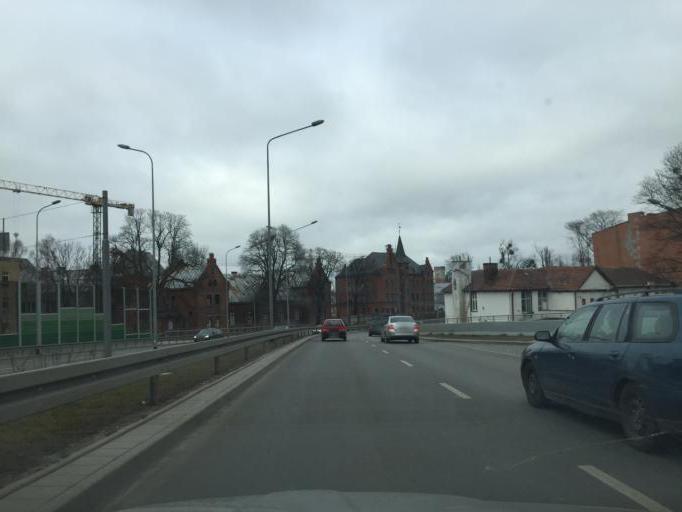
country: PL
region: Pomeranian Voivodeship
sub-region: Gdansk
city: Gdansk
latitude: 54.3798
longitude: 18.5898
